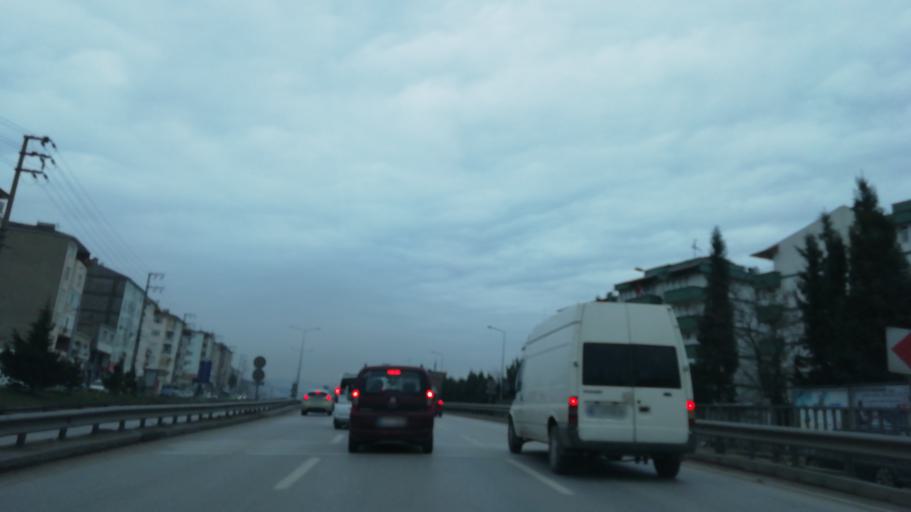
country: TR
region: Kocaeli
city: Derince
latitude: 40.7560
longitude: 29.8336
